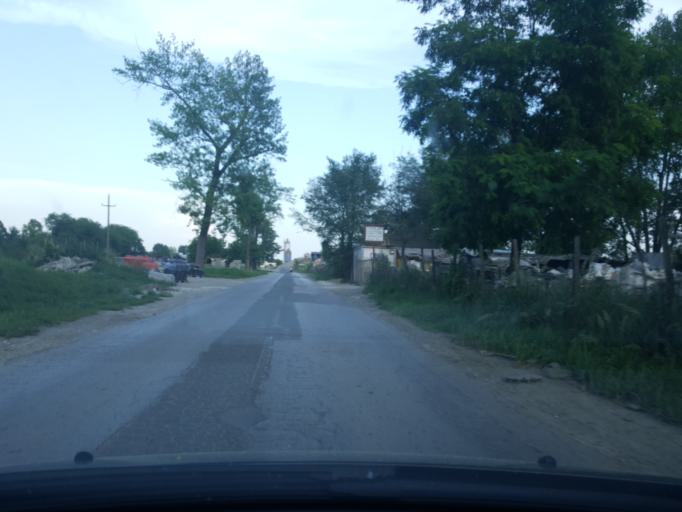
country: RS
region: Autonomna Pokrajina Vojvodina
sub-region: Juznobacki Okrug
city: Novi Sad
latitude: 45.2851
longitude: 19.8054
